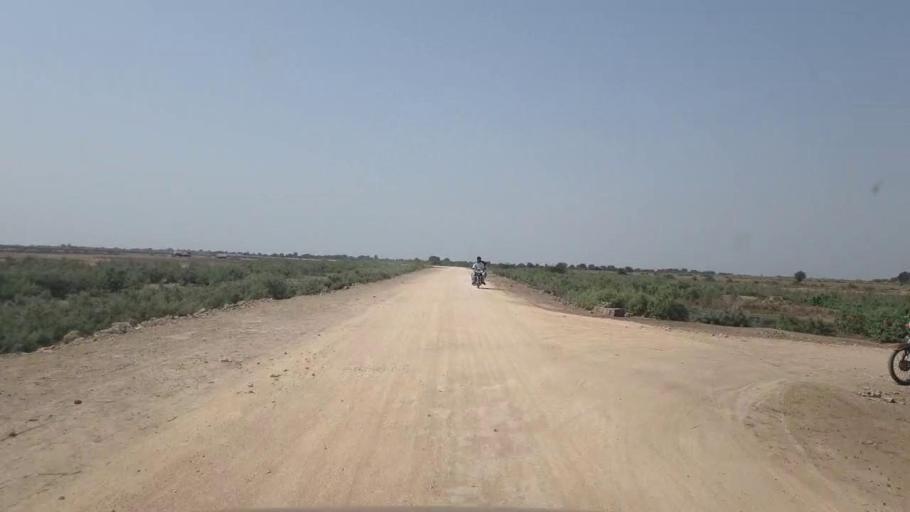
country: PK
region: Sindh
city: Jati
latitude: 24.3725
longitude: 68.5663
